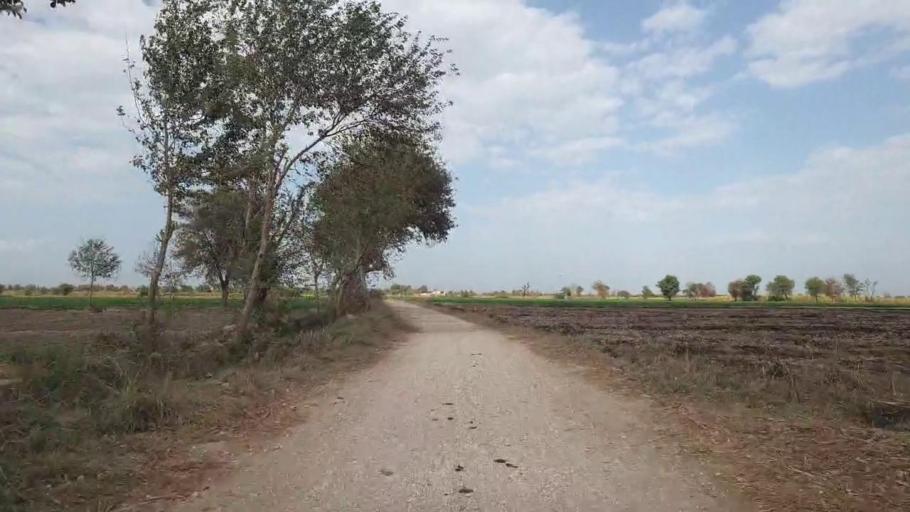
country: PK
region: Sindh
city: Shahdadpur
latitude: 25.9763
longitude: 68.4769
